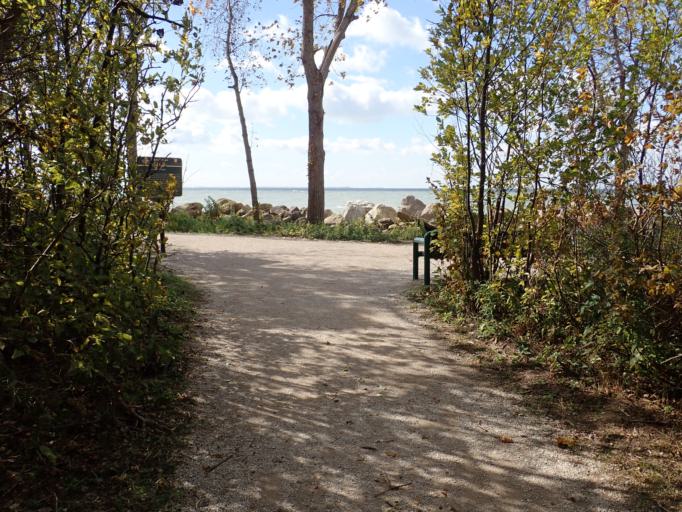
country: US
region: Ohio
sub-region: Erie County
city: Sandusky
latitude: 41.9121
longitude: -82.5094
